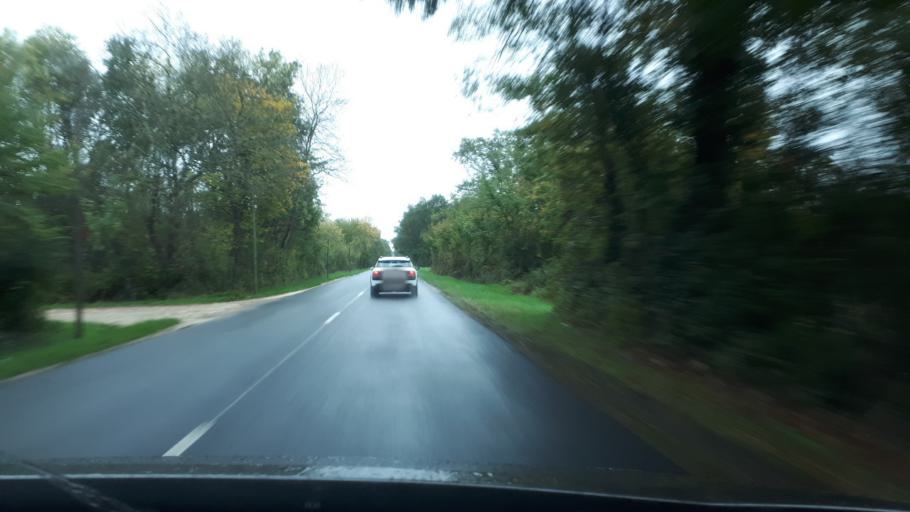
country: FR
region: Centre
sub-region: Departement du Loir-et-Cher
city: Gievres
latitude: 47.2720
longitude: 1.6632
